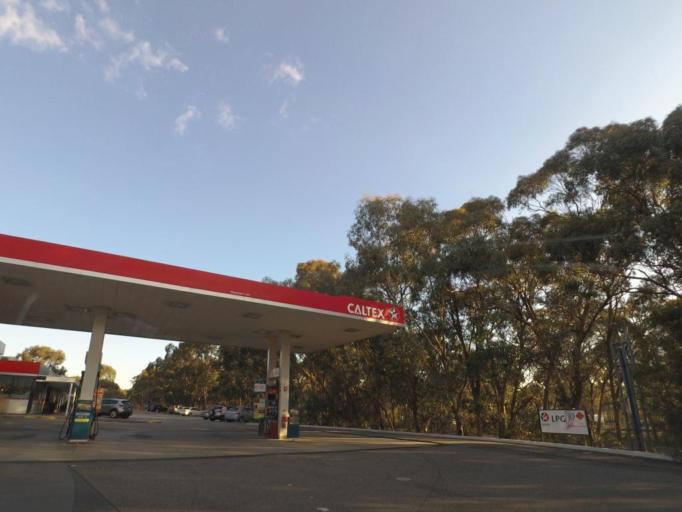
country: AU
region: Victoria
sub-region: Murrindindi
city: Kinglake West
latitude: -37.0629
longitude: 145.1019
